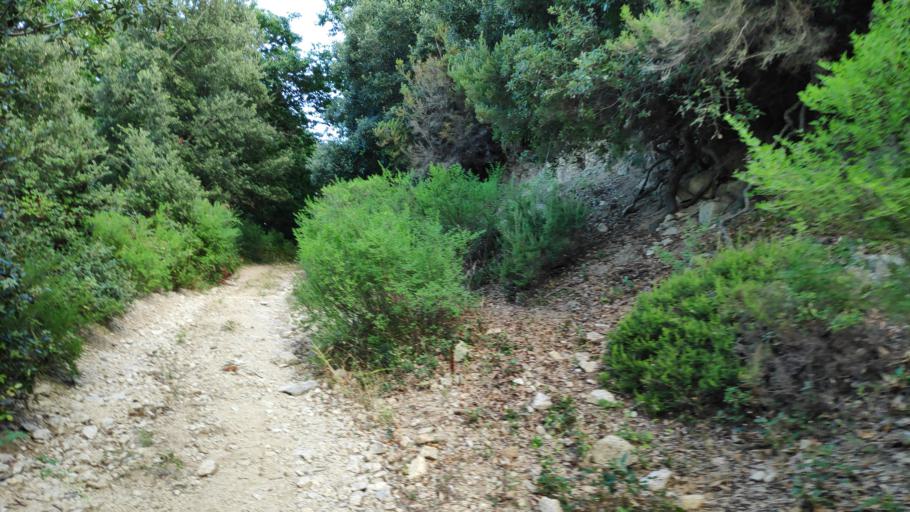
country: IT
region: Calabria
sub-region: Provincia di Reggio Calabria
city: Pazzano
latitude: 38.4734
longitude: 16.4118
